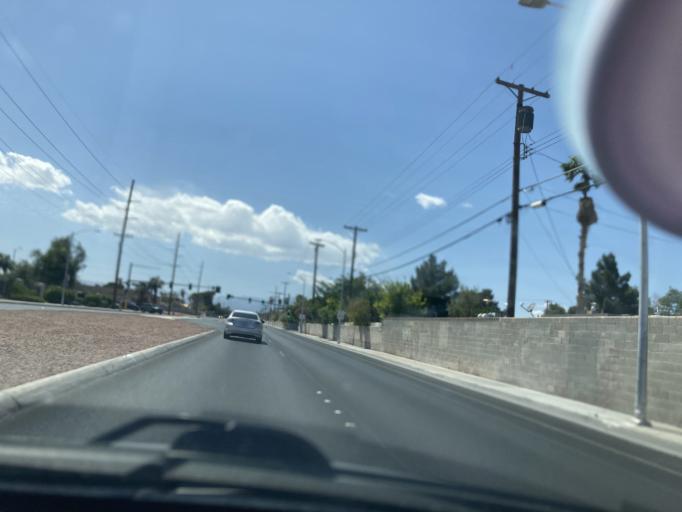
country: US
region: Nevada
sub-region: Clark County
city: North Las Vegas
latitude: 36.1811
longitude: -115.1057
